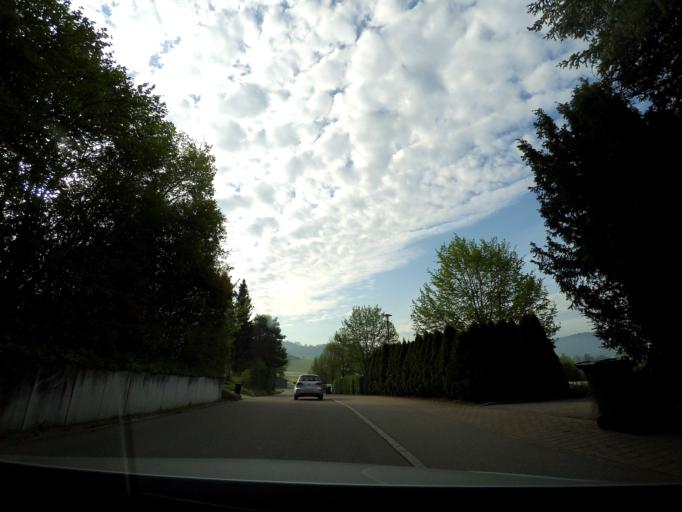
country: DE
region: Baden-Wuerttemberg
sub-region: Regierungsbezirk Stuttgart
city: Oberrot
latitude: 49.0139
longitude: 9.6756
